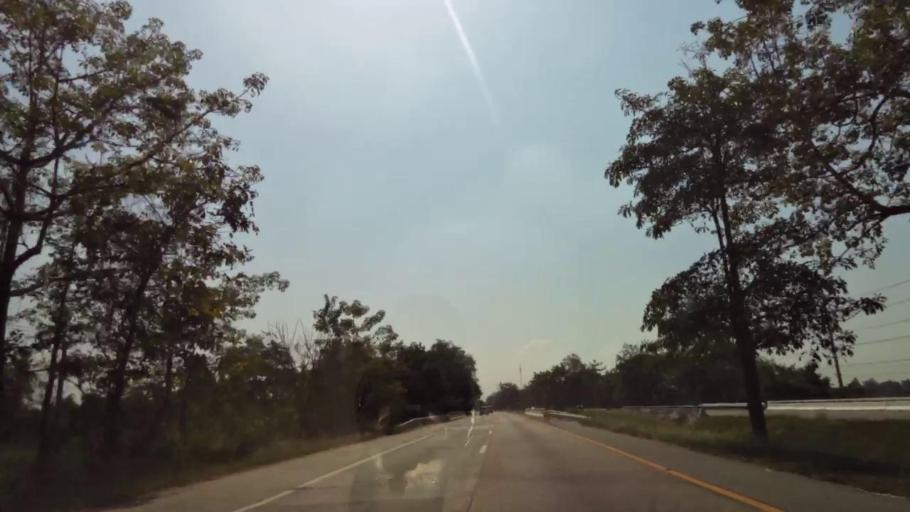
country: TH
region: Phichit
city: Wachira Barami
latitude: 16.6427
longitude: 100.1498
